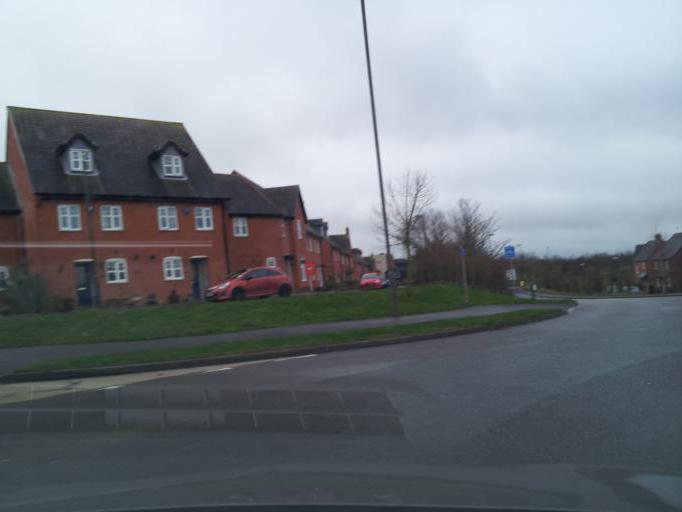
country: GB
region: England
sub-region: Derbyshire
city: Swadlincote
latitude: 52.7621
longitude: -1.5379
